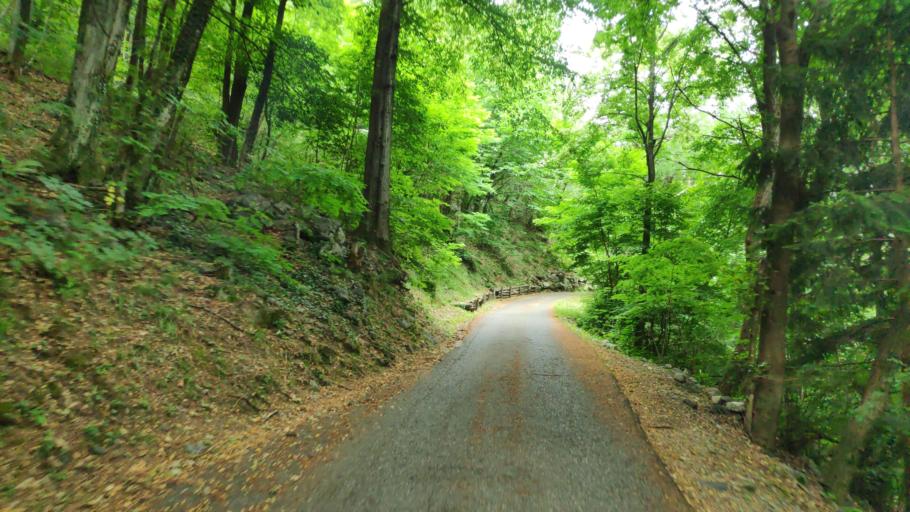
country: IT
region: Lombardy
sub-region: Provincia di Sondrio
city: Prata Centro
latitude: 46.3023
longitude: 9.4029
